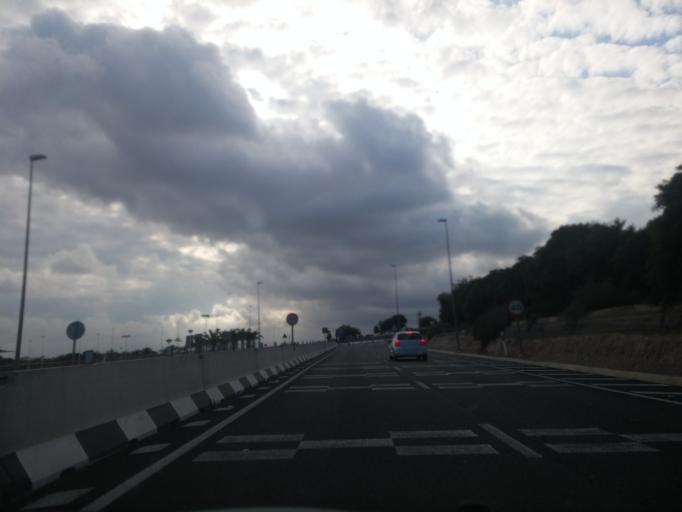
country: ES
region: Valencia
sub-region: Provincia de Alicante
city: Alicante
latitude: 38.2969
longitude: -0.5754
